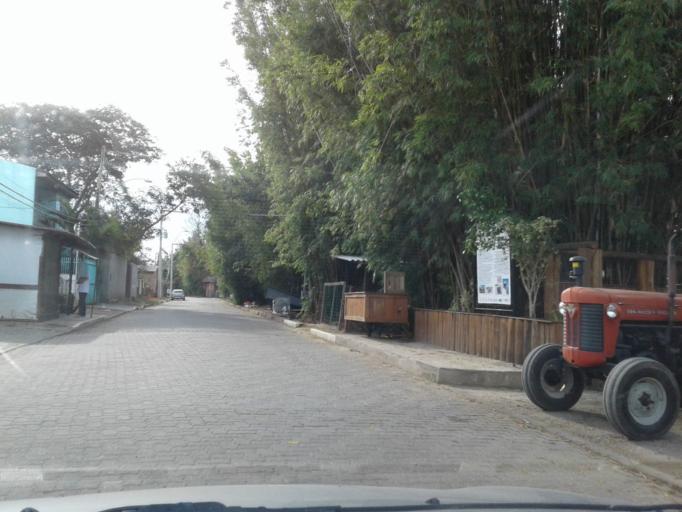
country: BR
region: Rio Grande do Sul
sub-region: Porto Alegre
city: Porto Alegre
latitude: -30.0189
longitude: -51.2564
